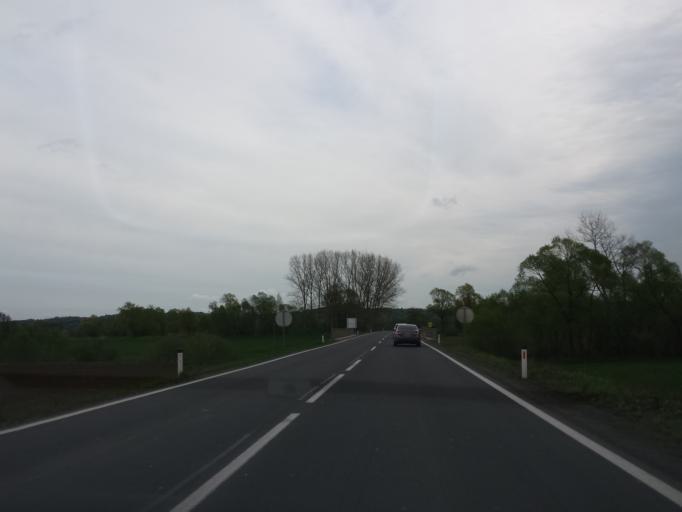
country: AT
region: Styria
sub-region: Politischer Bezirk Hartberg-Fuerstenfeld
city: Fuerstenfeld
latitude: 47.0518
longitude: 16.0962
